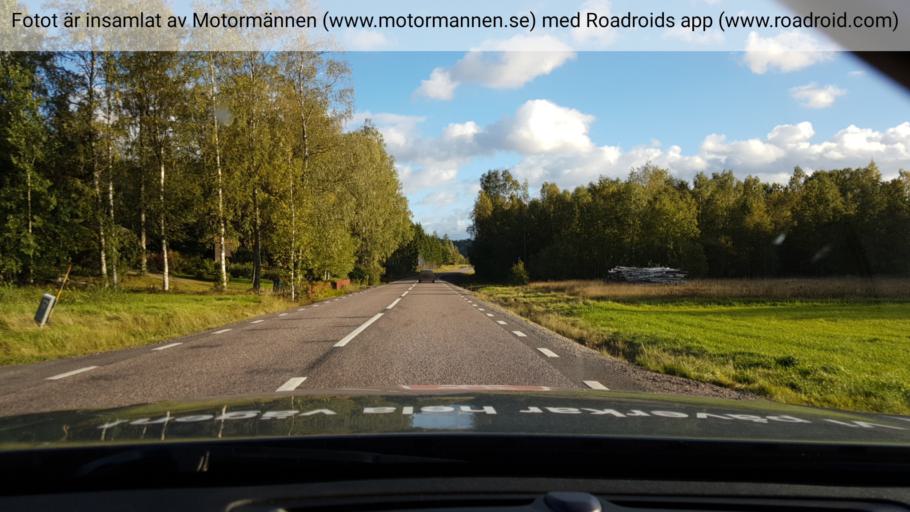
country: SE
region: Vaermland
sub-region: Karlstads Kommun
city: Molkom
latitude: 59.6750
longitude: 13.6865
